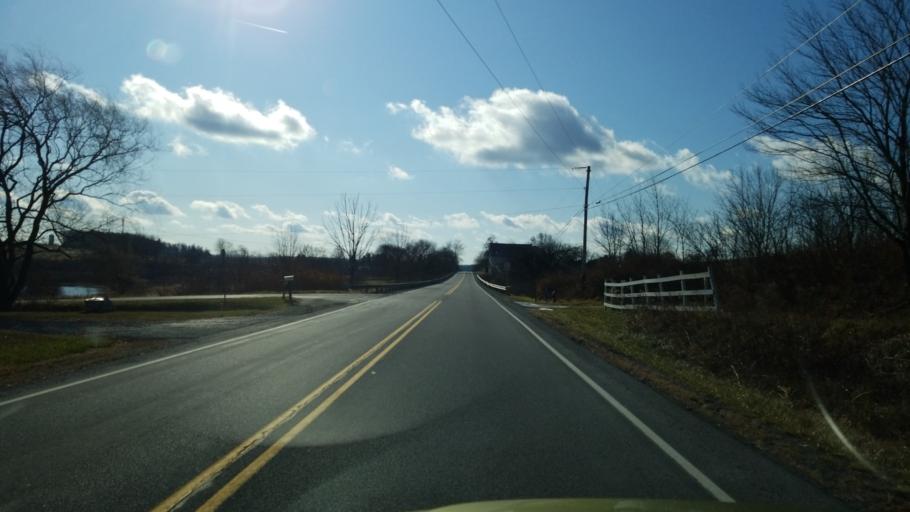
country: US
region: Pennsylvania
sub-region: Clearfield County
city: Hyde
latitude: 40.9967
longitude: -78.4419
